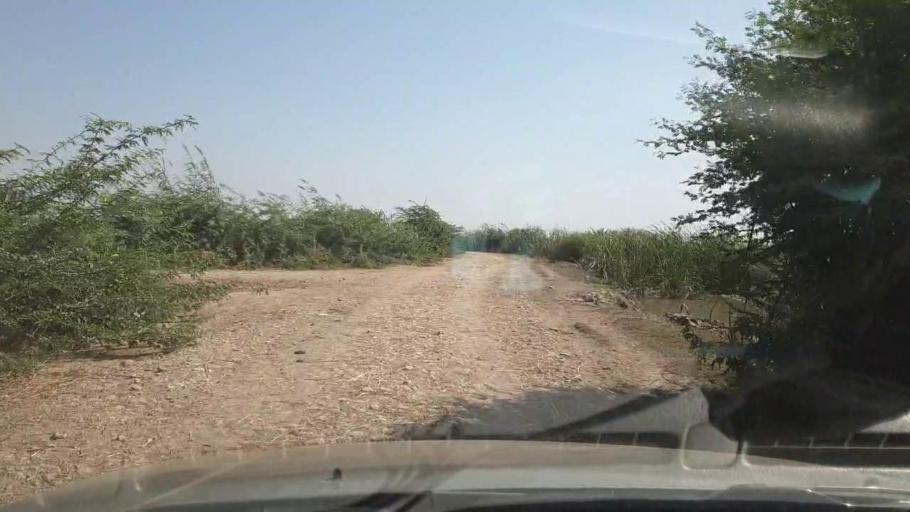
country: PK
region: Sindh
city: Daro Mehar
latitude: 24.9729
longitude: 68.1130
